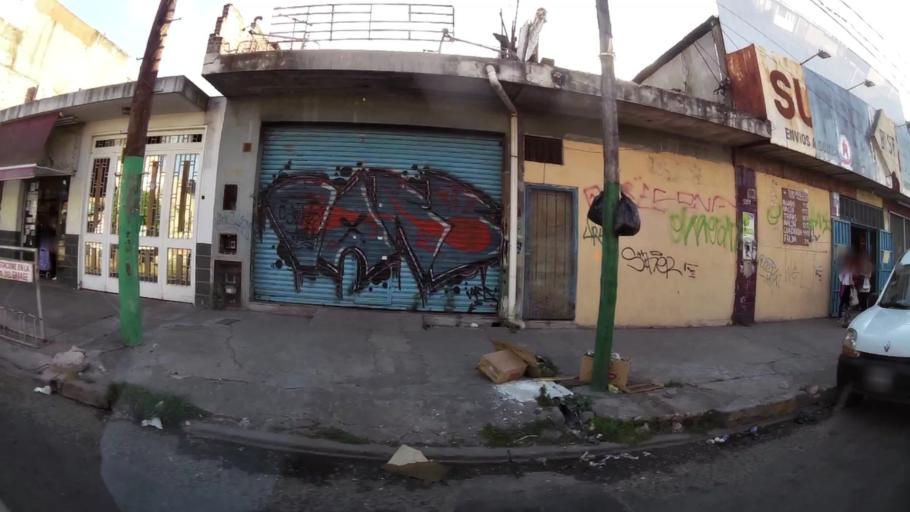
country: AR
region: Buenos Aires
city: Hurlingham
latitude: -34.5726
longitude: -58.6125
